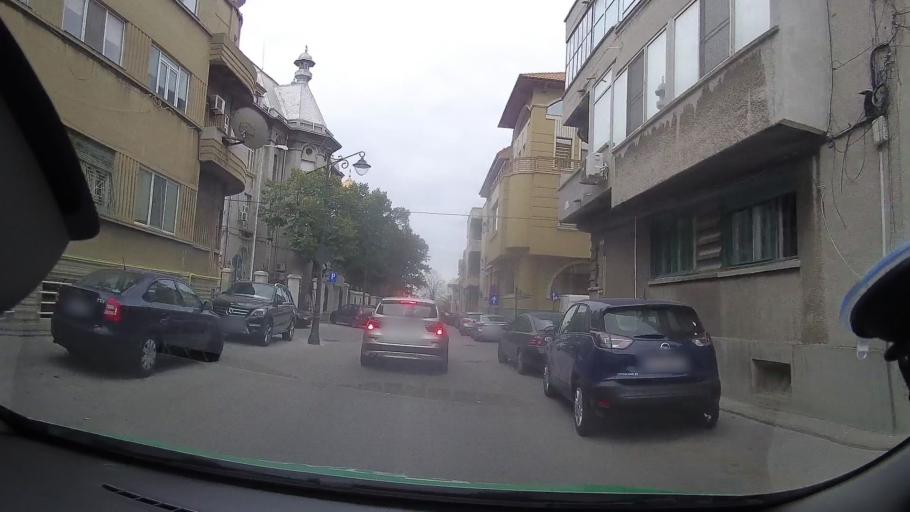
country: RO
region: Constanta
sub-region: Municipiul Constanta
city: Constanta
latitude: 44.1720
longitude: 28.6603
